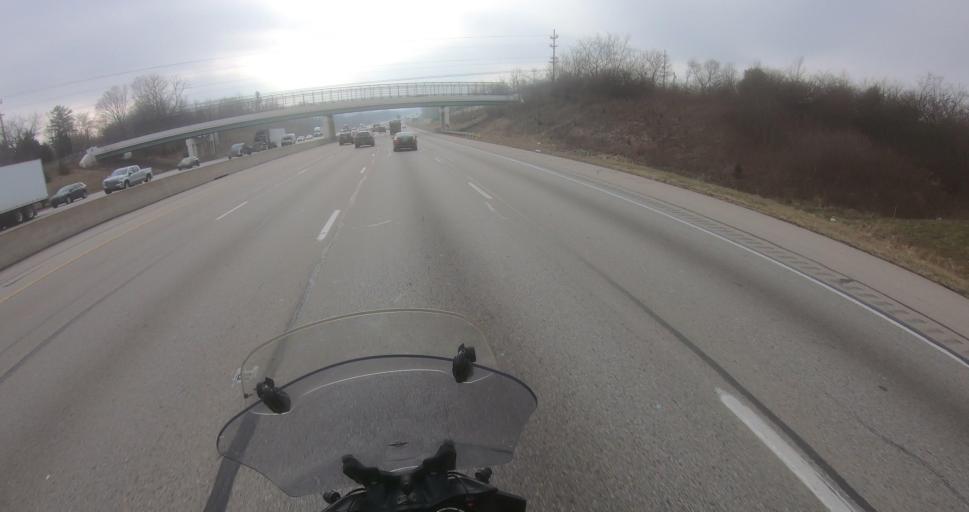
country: US
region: Ohio
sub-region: Warren County
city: Franklin
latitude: 39.5541
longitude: -84.2796
